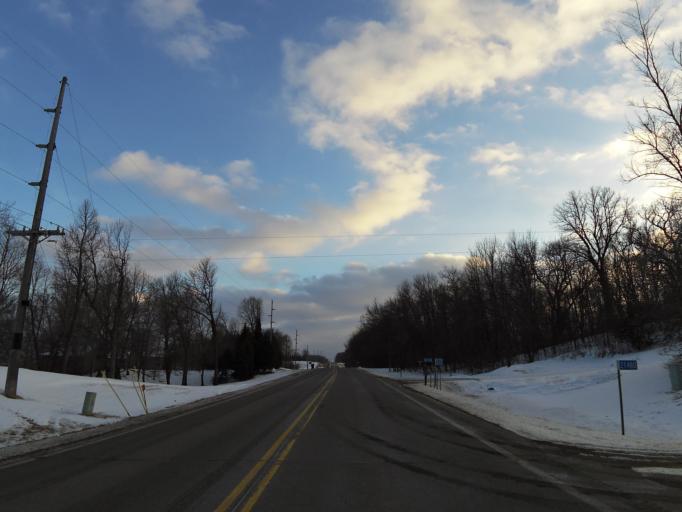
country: US
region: Minnesota
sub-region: Scott County
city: Prior Lake
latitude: 44.6382
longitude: -93.4404
